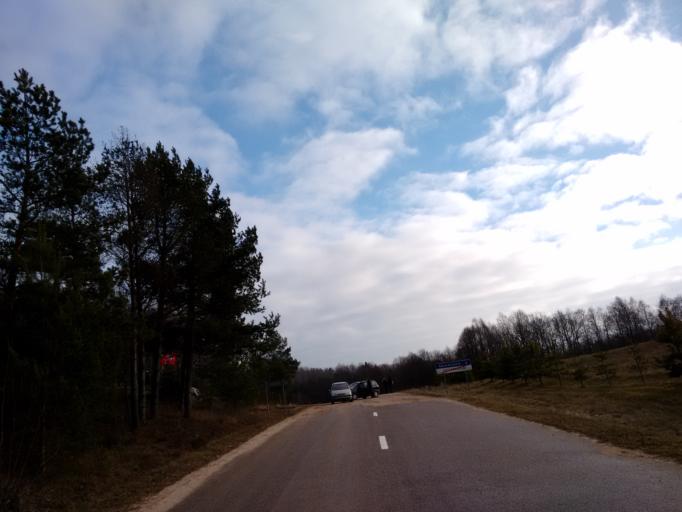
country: LT
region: Alytaus apskritis
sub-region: Alytus
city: Alytus
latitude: 54.2460
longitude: 23.9316
